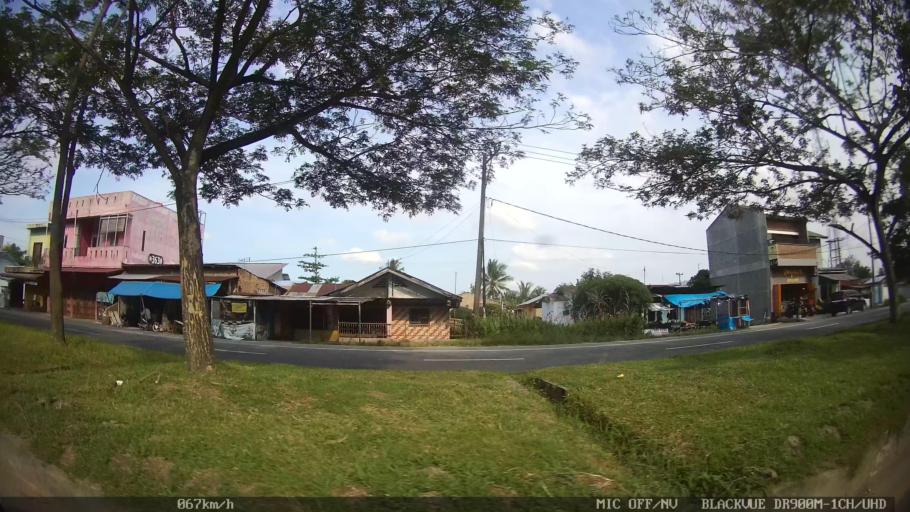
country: ID
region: North Sumatra
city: Percut
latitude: 3.5766
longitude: 98.8009
